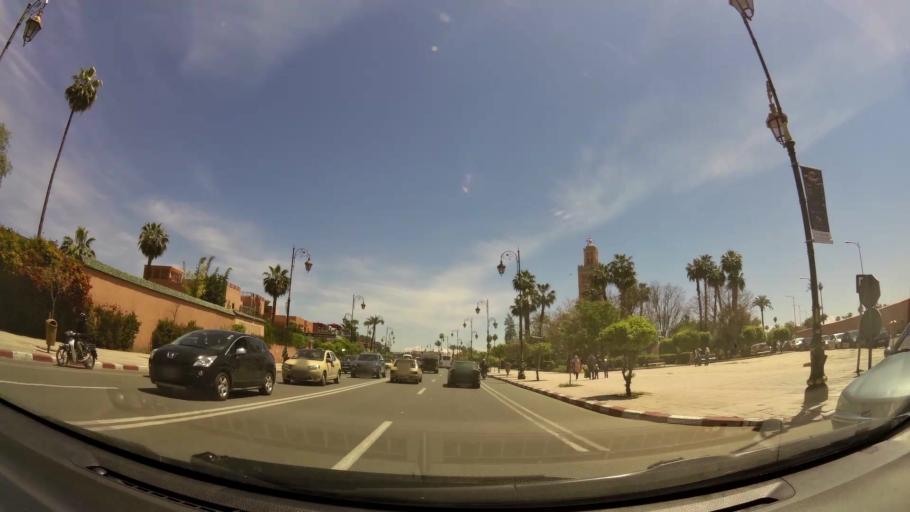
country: MA
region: Marrakech-Tensift-Al Haouz
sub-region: Marrakech
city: Marrakesh
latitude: 31.6259
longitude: -7.9949
